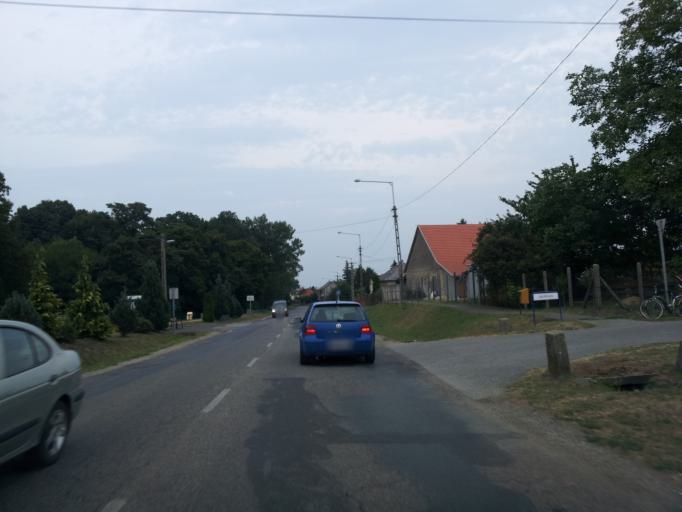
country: HU
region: Vas
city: Vep
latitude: 47.2285
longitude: 16.7140
